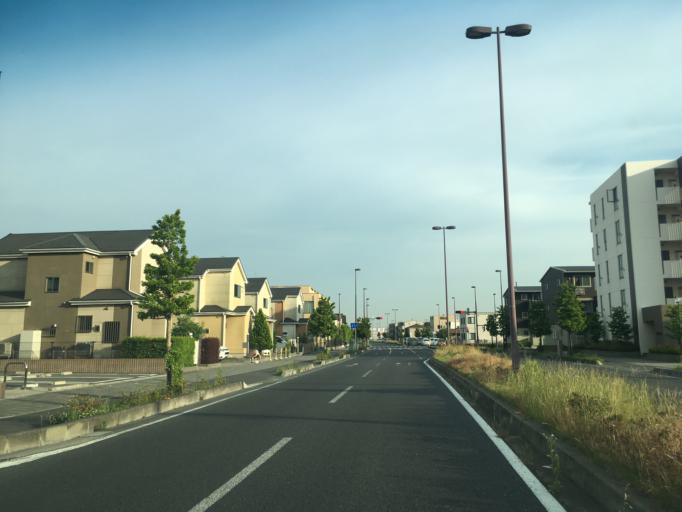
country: JP
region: Saitama
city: Yoshikawa
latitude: 35.8827
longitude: 139.8155
